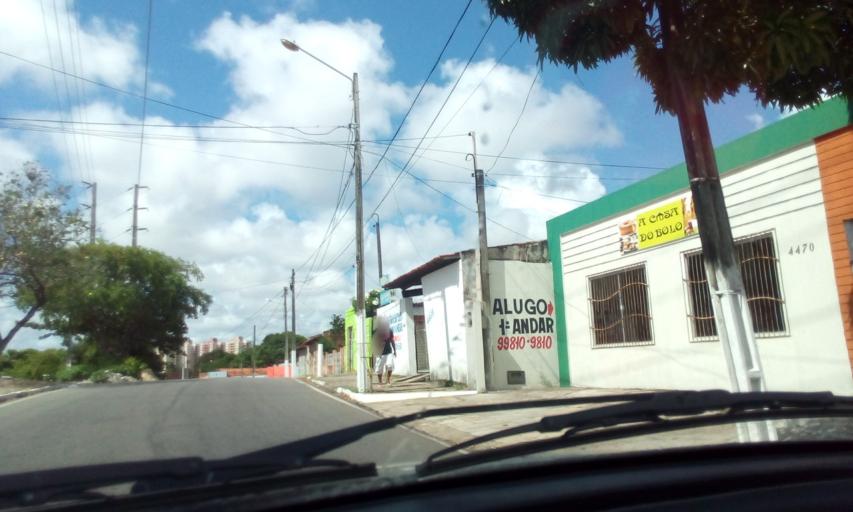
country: BR
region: Rio Grande do Norte
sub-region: Parnamirim
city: Parnamirim
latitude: -5.8736
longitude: -35.2090
